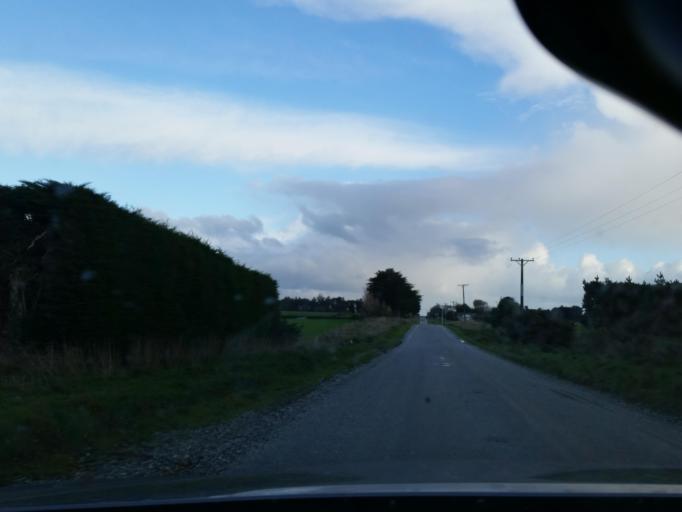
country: NZ
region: Southland
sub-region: Invercargill City
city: Invercargill
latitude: -46.4112
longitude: 168.5060
